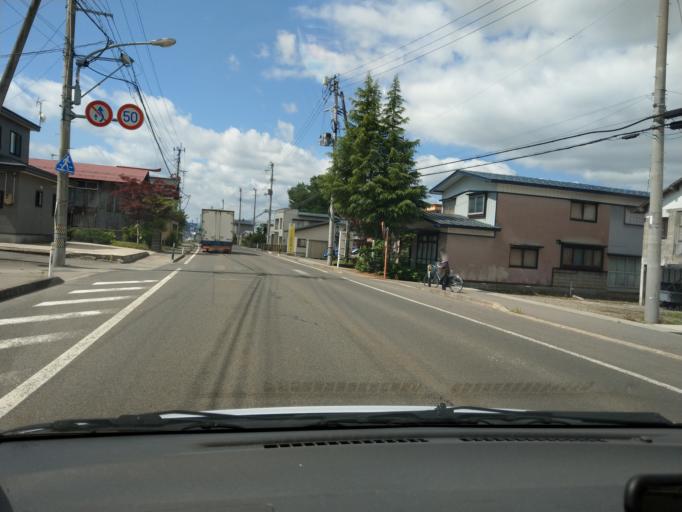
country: JP
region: Akita
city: Yuzawa
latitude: 39.1961
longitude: 140.5037
